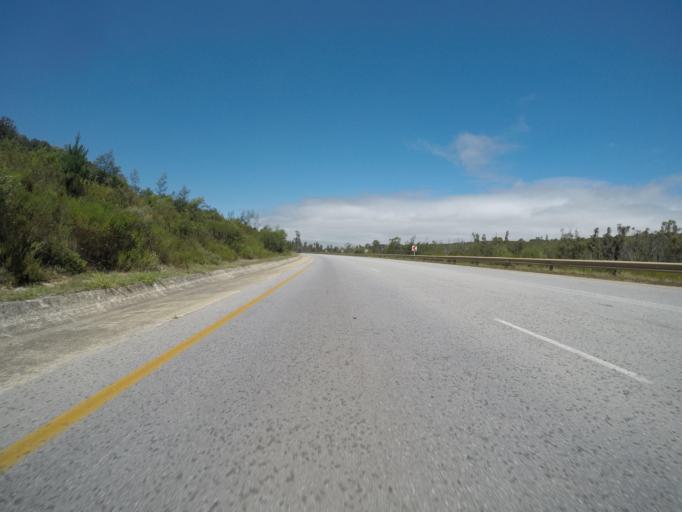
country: ZA
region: Eastern Cape
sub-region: Cacadu District Municipality
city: Jeffrey's Bay
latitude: -33.9030
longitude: 25.1014
